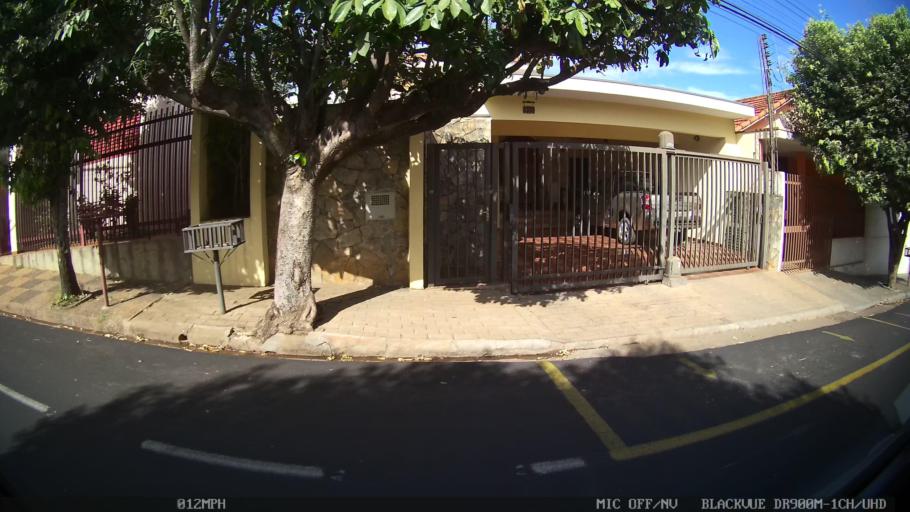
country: BR
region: Sao Paulo
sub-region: Catanduva
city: Catanduva
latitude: -21.1248
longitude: -48.9743
